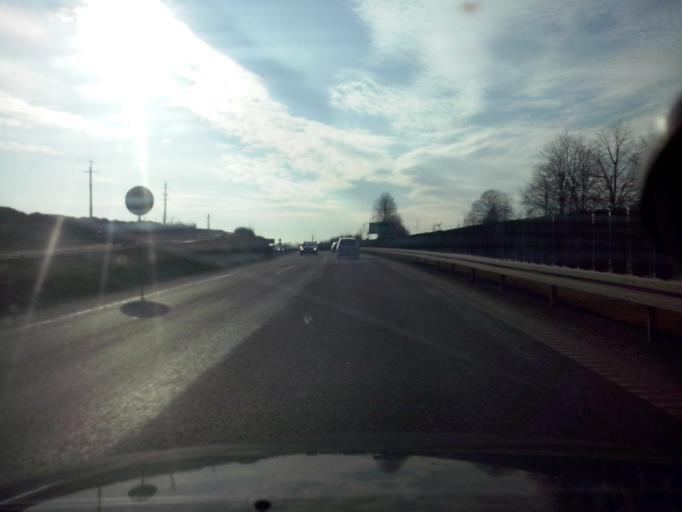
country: PL
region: Subcarpathian Voivodeship
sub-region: Powiat rzeszowski
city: Wolka Podlesna
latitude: 50.1542
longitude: 22.0780
